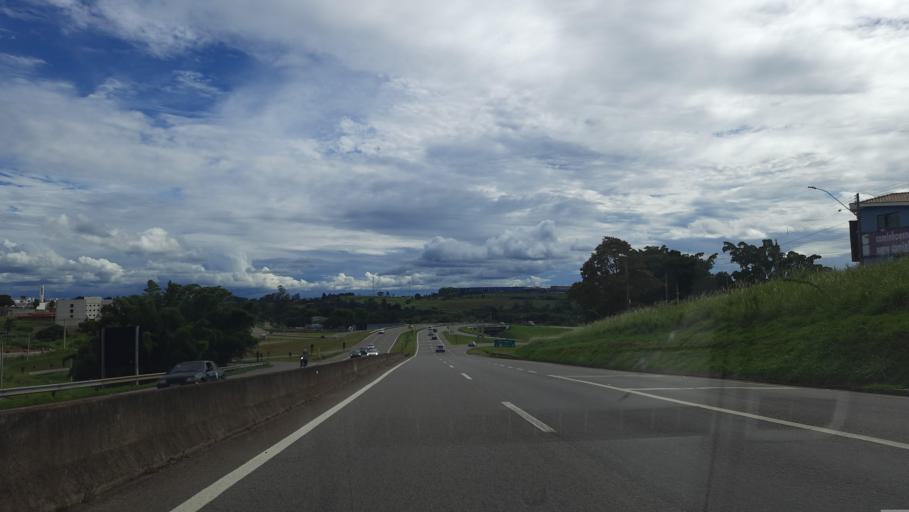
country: BR
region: Sao Paulo
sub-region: Sao Joao Da Boa Vista
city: Sao Joao da Boa Vista
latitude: -21.9890
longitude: -46.7910
